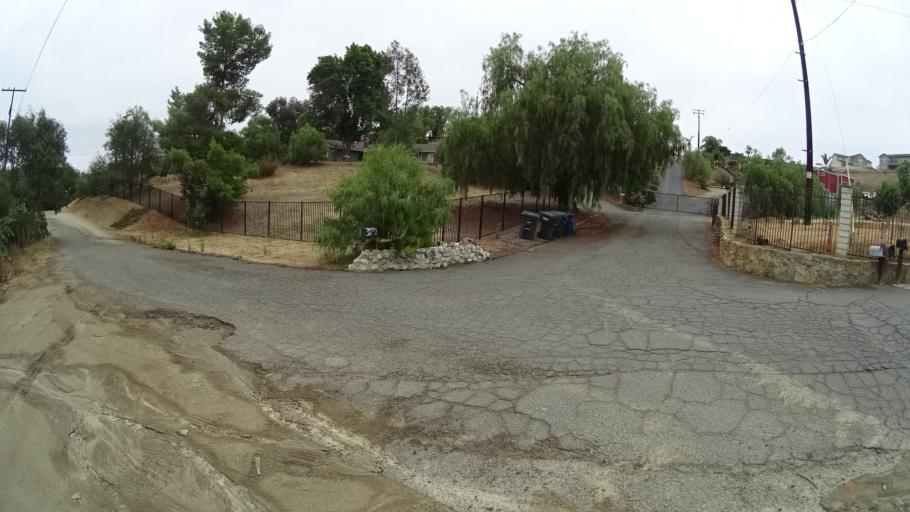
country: US
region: California
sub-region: San Diego County
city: San Marcos
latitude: 33.1130
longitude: -117.1354
